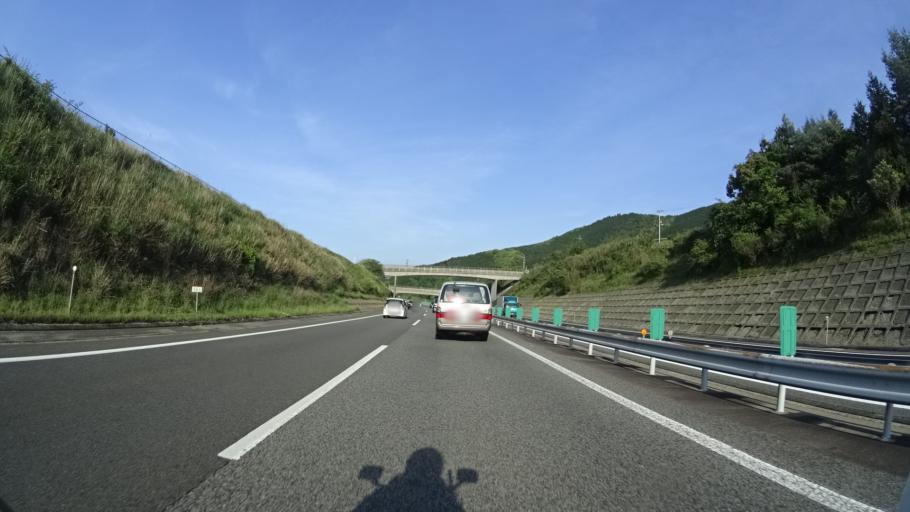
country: JP
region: Ehime
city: Kawanoecho
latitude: 33.9595
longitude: 133.4913
